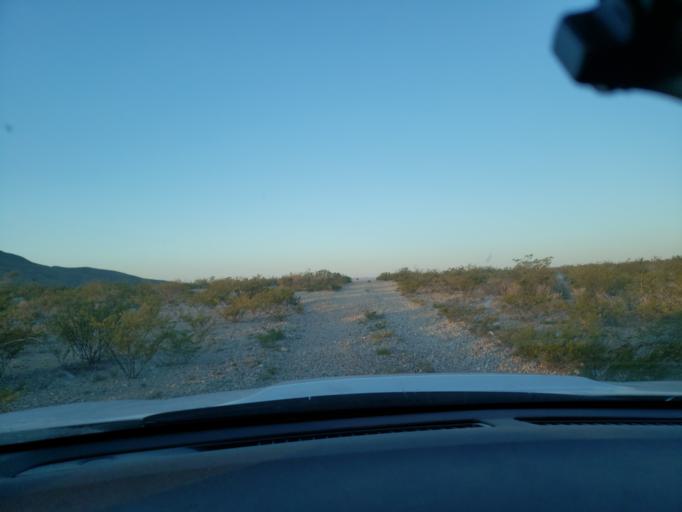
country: US
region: Texas
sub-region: Culberson County
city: Van Horn
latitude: 30.7194
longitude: -104.7691
